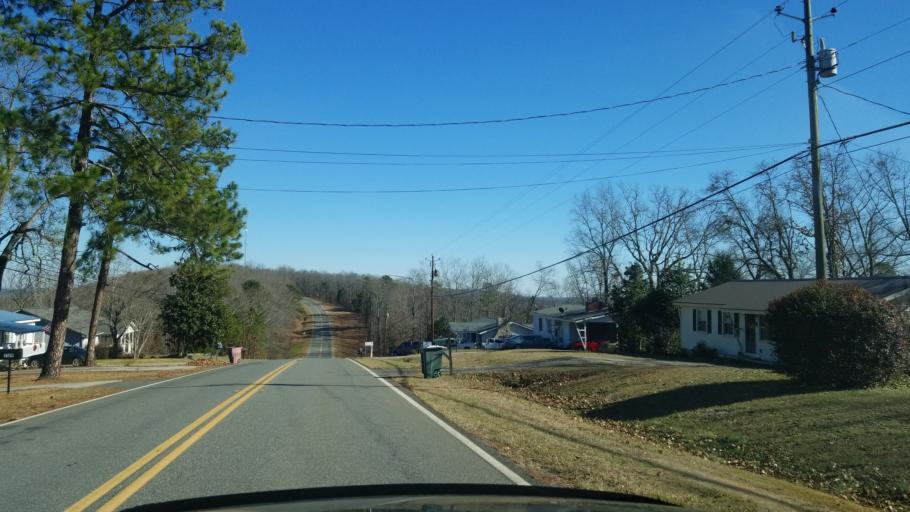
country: US
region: Georgia
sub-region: Meriwether County
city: Manchester
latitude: 32.8437
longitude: -84.6323
